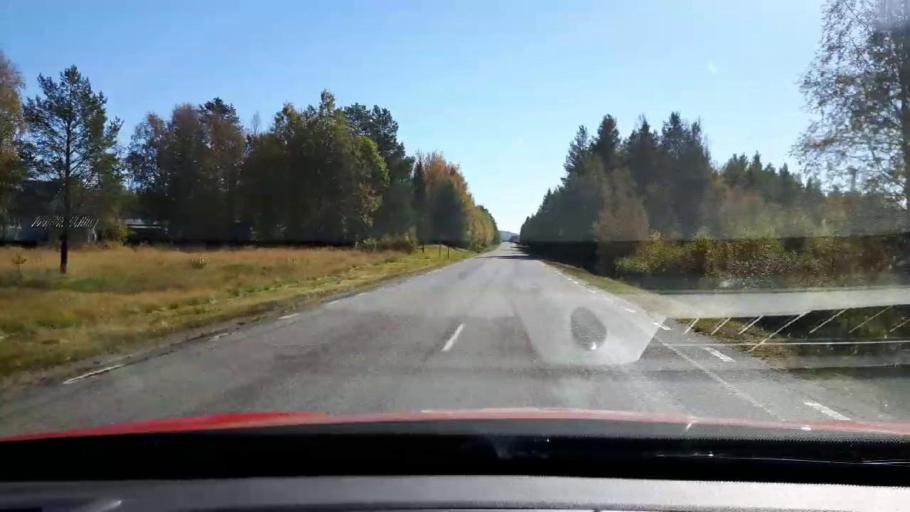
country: SE
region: Jaemtland
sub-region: Harjedalens Kommun
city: Sveg
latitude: 62.3090
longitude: 14.0429
